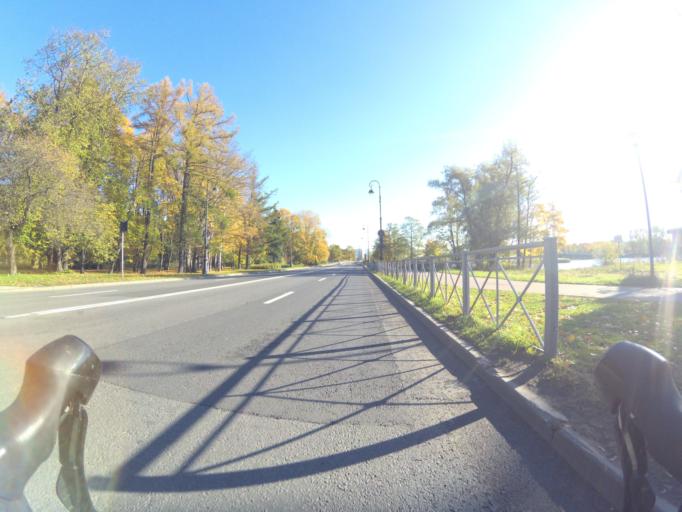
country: RU
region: Leningrad
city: Krestovskiy ostrov
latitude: 59.9671
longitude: 30.2505
